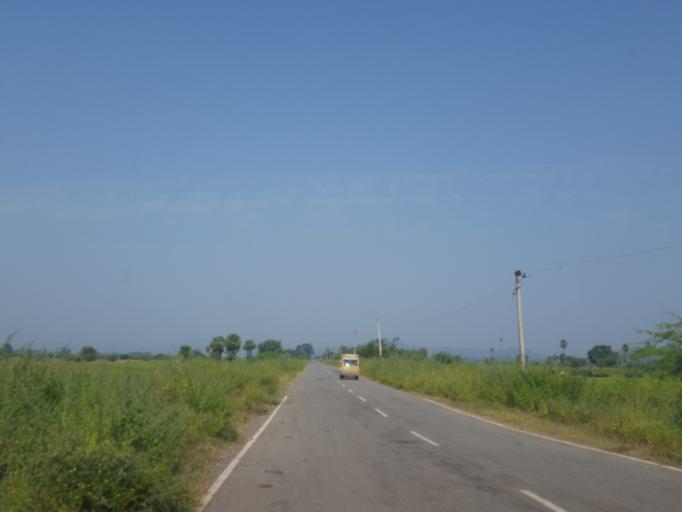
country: IN
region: Telangana
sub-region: Khammam
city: Yellandu
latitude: 17.6437
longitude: 80.2964
